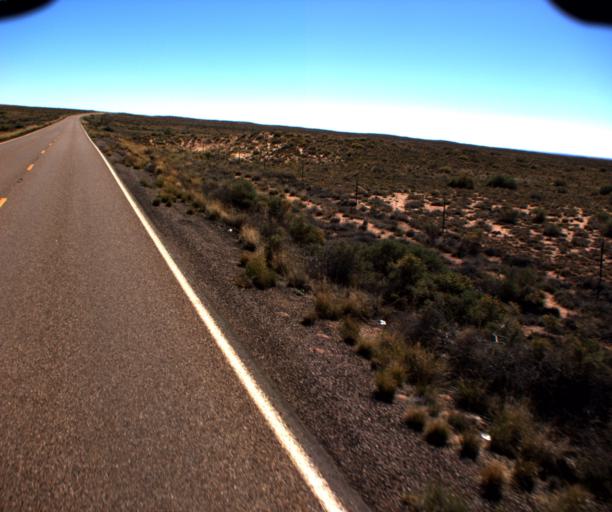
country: US
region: Arizona
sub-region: Navajo County
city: Holbrook
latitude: 35.0419
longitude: -110.0925
